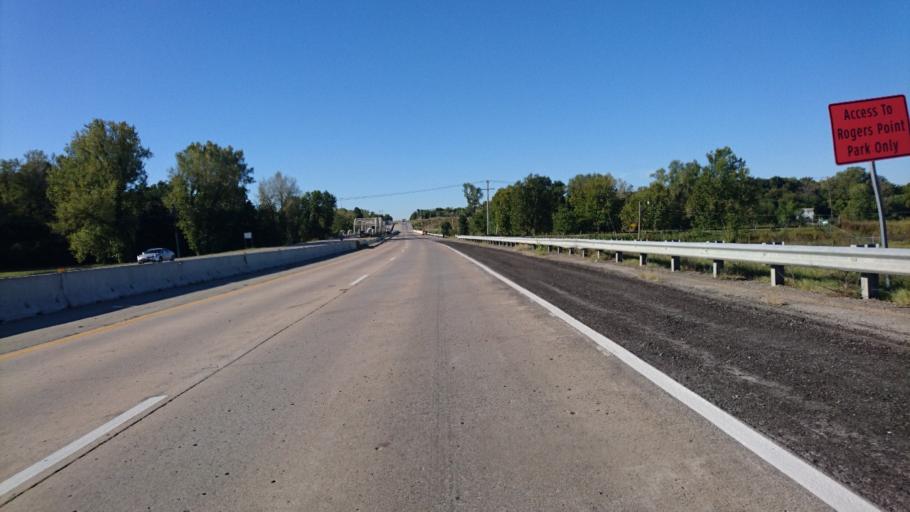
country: US
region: Oklahoma
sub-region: Rogers County
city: Catoosa
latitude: 36.2122
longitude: -95.7235
